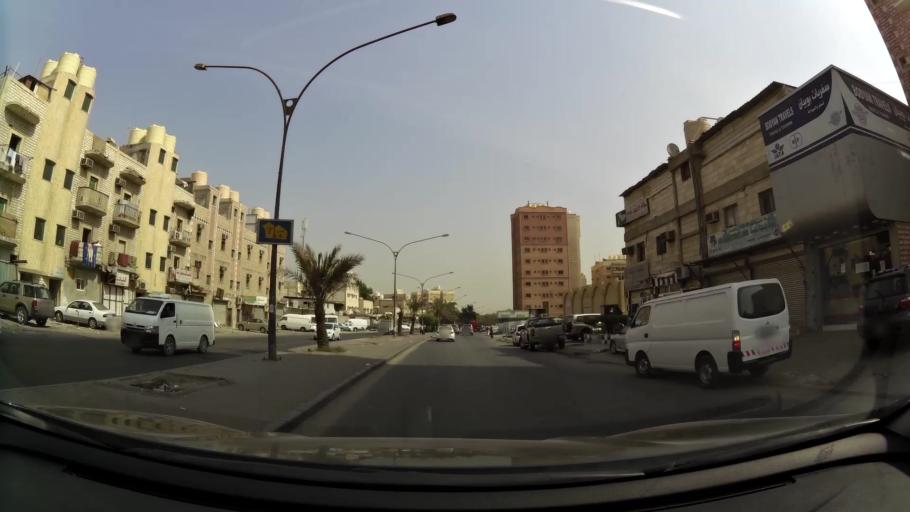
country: KW
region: Al Farwaniyah
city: Al Farwaniyah
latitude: 29.2586
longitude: 47.9301
